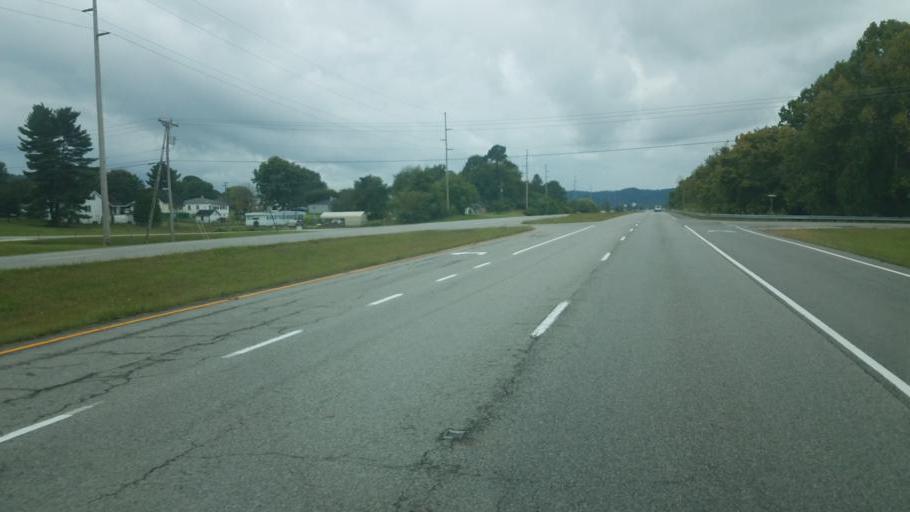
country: US
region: Ohio
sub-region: Scioto County
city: New Boston
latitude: 38.7327
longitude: -82.9134
